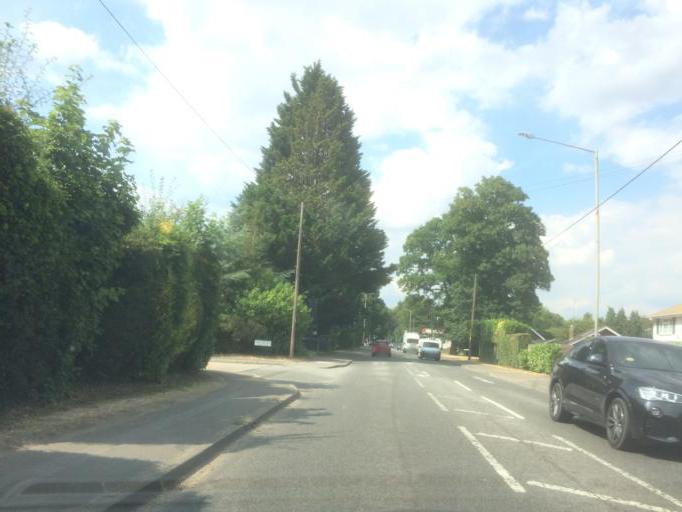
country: GB
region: England
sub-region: Buckinghamshire
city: Farnham Royal
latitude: 51.5588
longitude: -0.6154
